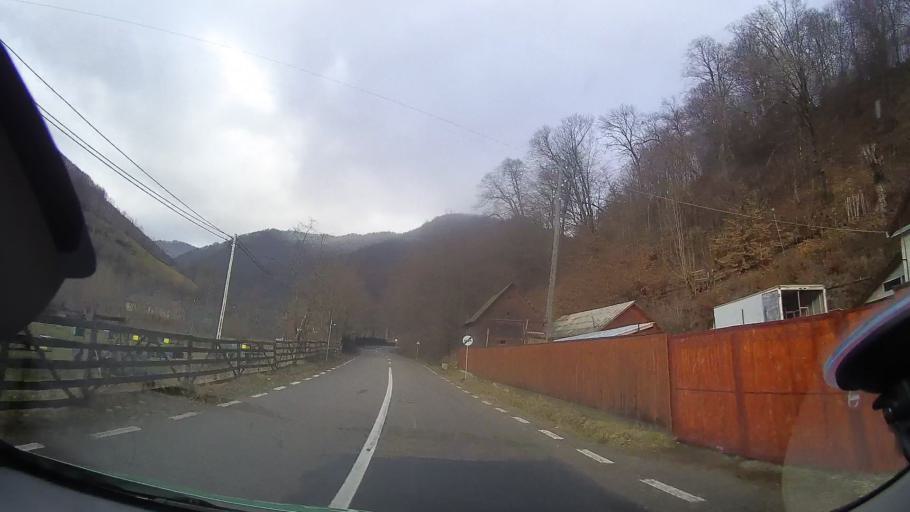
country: RO
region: Cluj
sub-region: Comuna Valea Ierii
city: Valea Ierii
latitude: 46.6457
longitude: 23.3494
